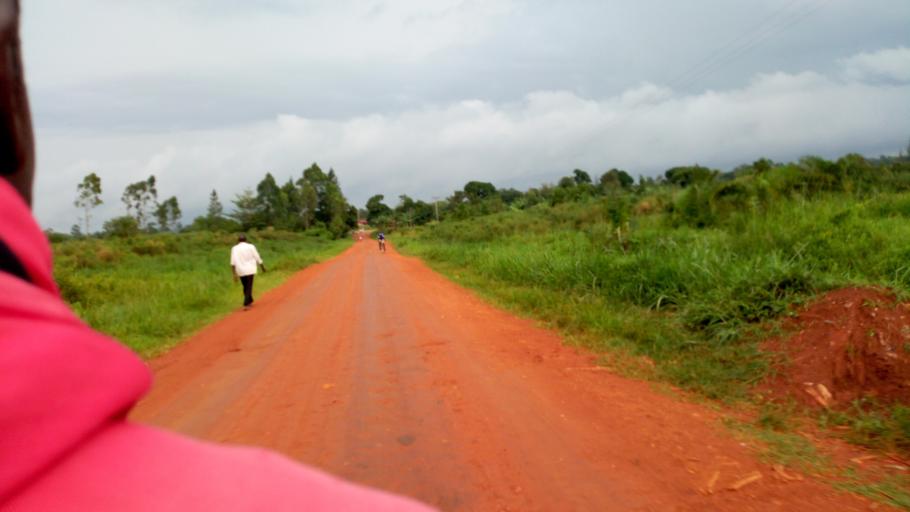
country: UG
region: Western Region
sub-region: Masindi District
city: Masindi
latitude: 1.6728
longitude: 31.7322
